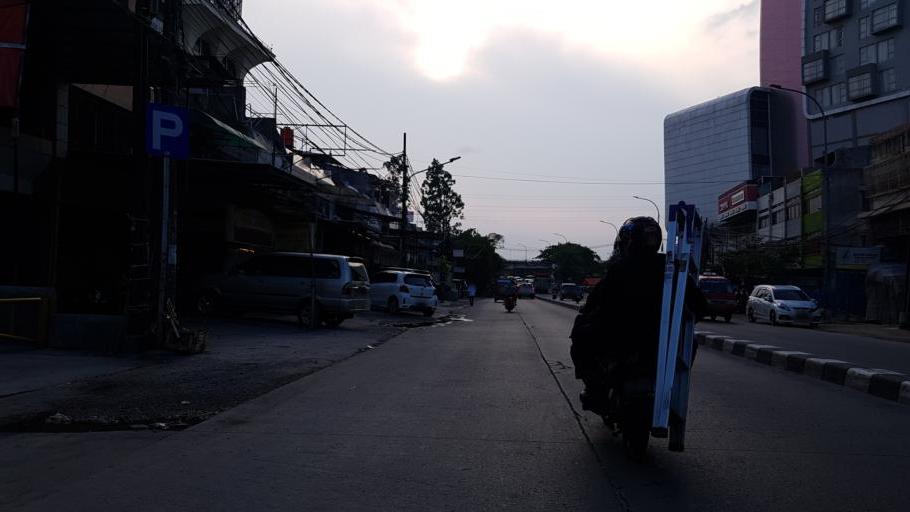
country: ID
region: Jakarta Raya
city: Jakarta
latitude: -6.1376
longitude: 106.7889
